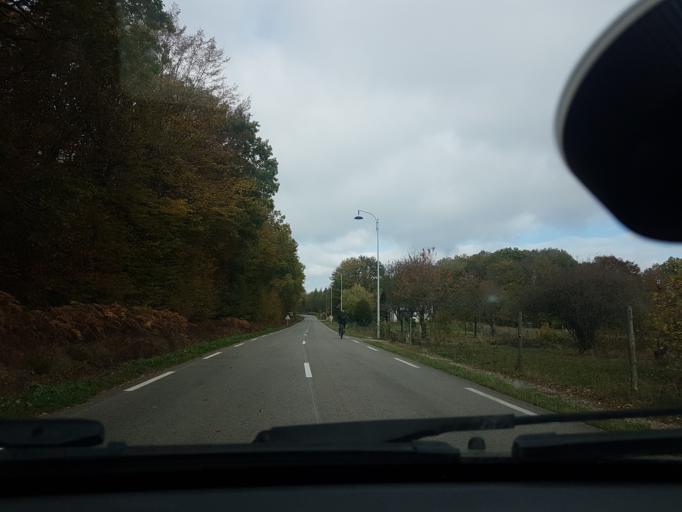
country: FR
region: Franche-Comte
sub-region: Departement de la Haute-Saone
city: Frahier-et-Chatebier
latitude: 47.6894
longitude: 6.7362
